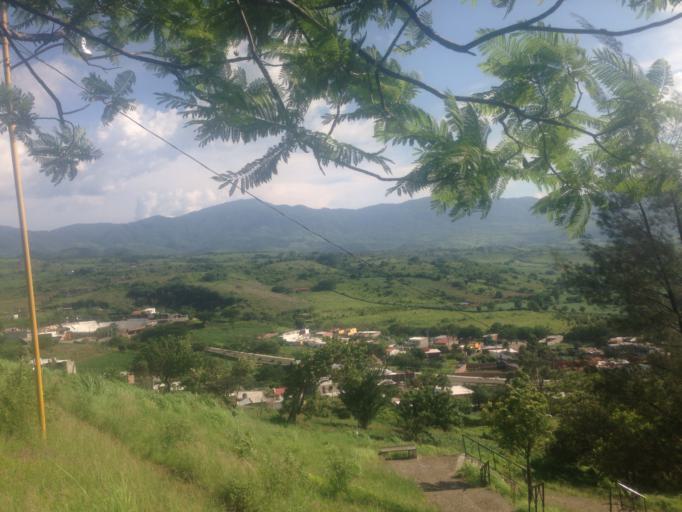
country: MX
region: Nayarit
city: Ixtlan del Rio
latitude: 21.0352
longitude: -104.3591
